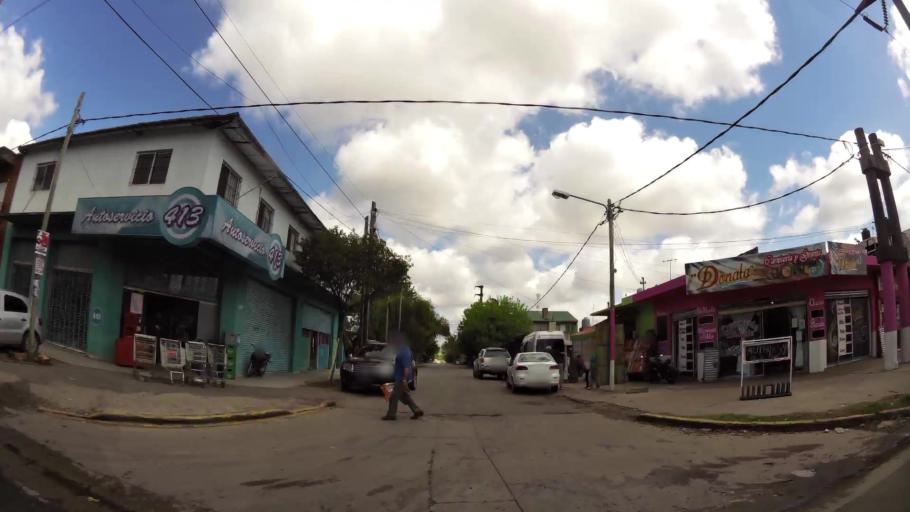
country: AR
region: Buenos Aires
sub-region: Partido de Quilmes
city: Quilmes
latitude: -34.8354
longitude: -58.1864
